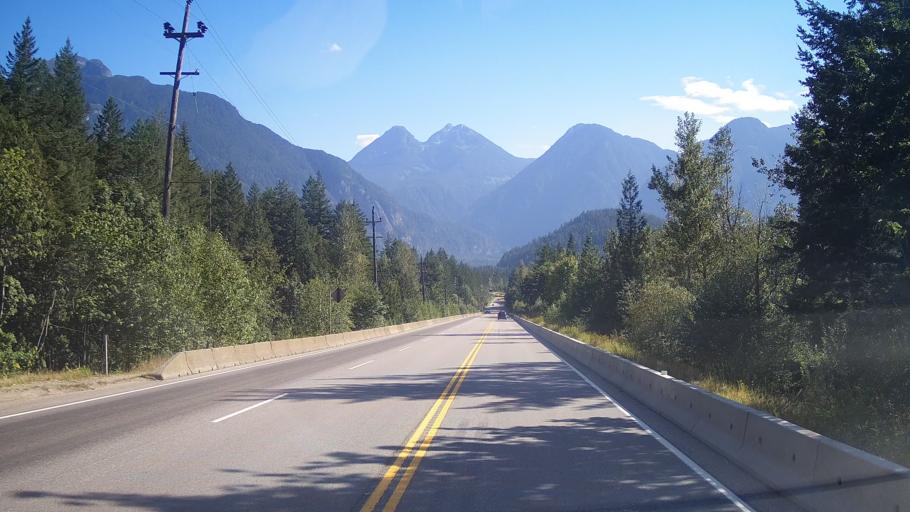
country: CA
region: British Columbia
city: Hope
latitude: 49.4057
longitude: -121.4543
